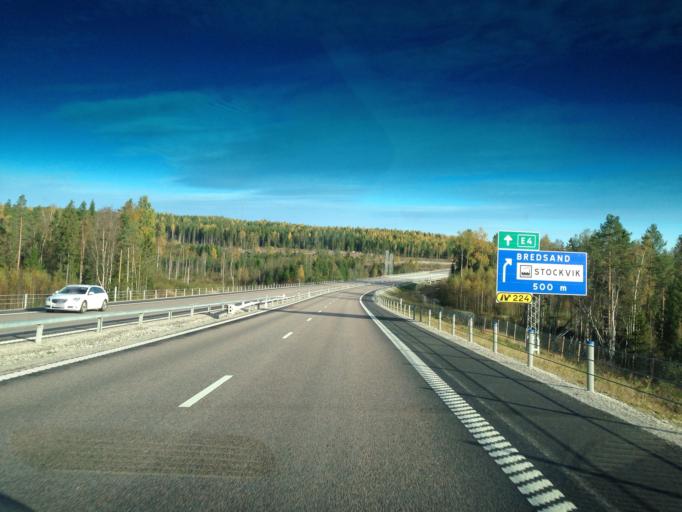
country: SE
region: Vaesternorrland
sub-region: Sundsvalls Kommun
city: Stockvik
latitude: 62.3301
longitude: 17.3458
